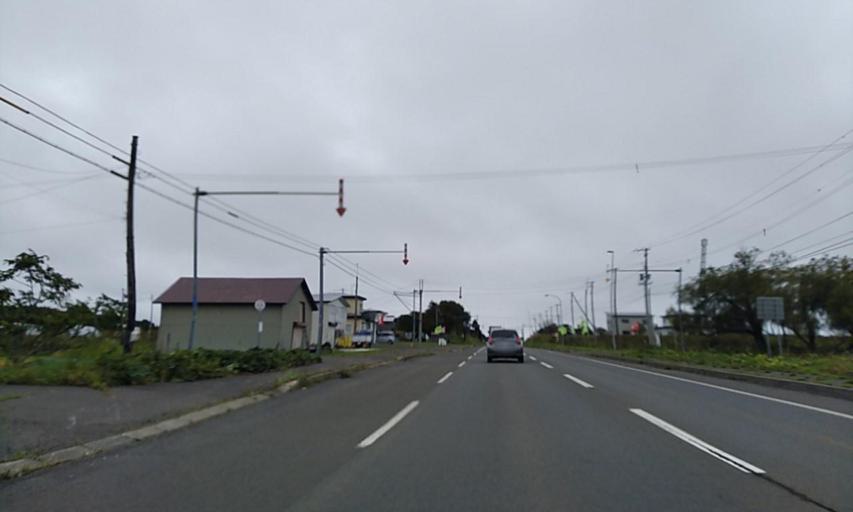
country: JP
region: Hokkaido
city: Nemuro
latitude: 43.2691
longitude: 145.4779
